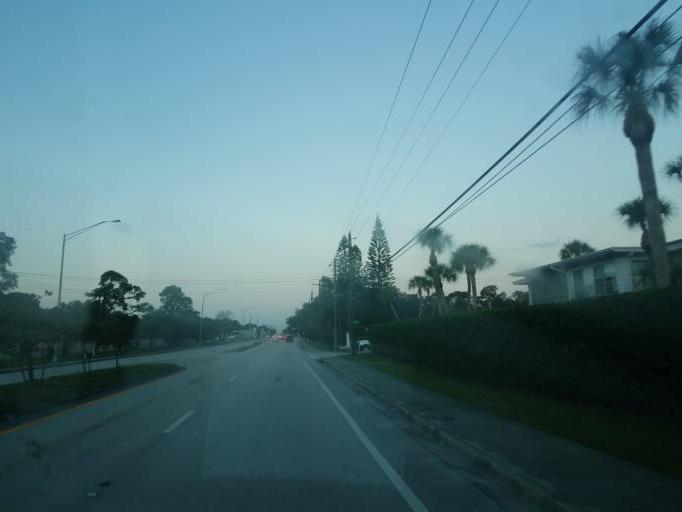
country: US
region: Florida
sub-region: Sarasota County
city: Kensington Park
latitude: 27.3524
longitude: -82.4936
